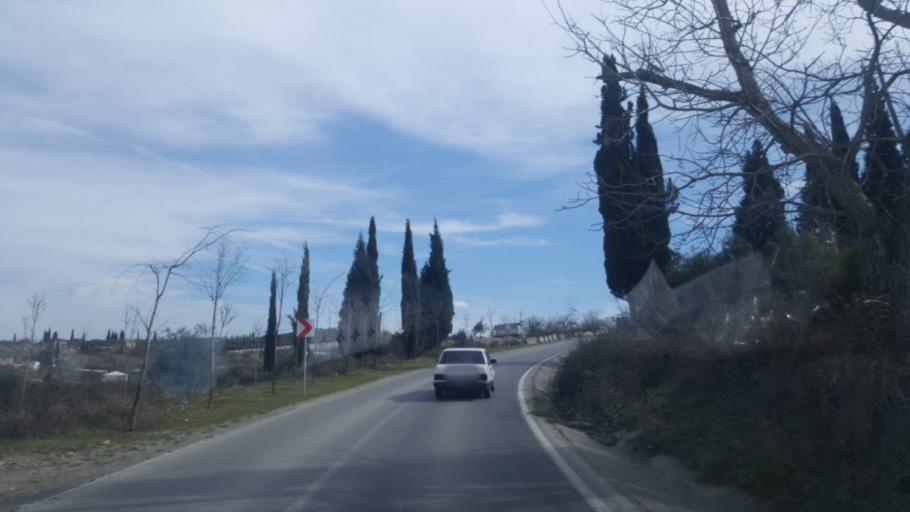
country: TR
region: Kocaeli
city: Tavsancil
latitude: 40.7882
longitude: 29.5715
